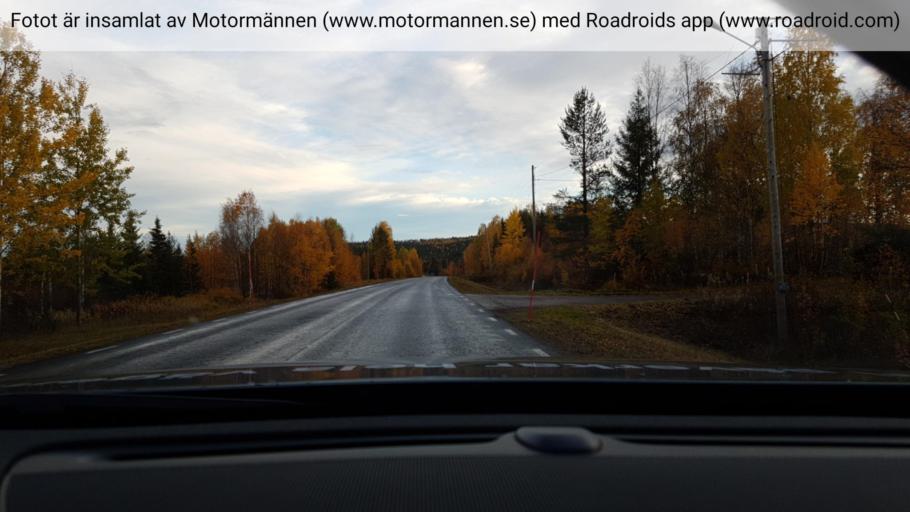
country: SE
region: Norrbotten
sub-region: Overkalix Kommun
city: OEverkalix
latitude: 66.9333
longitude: 22.7361
